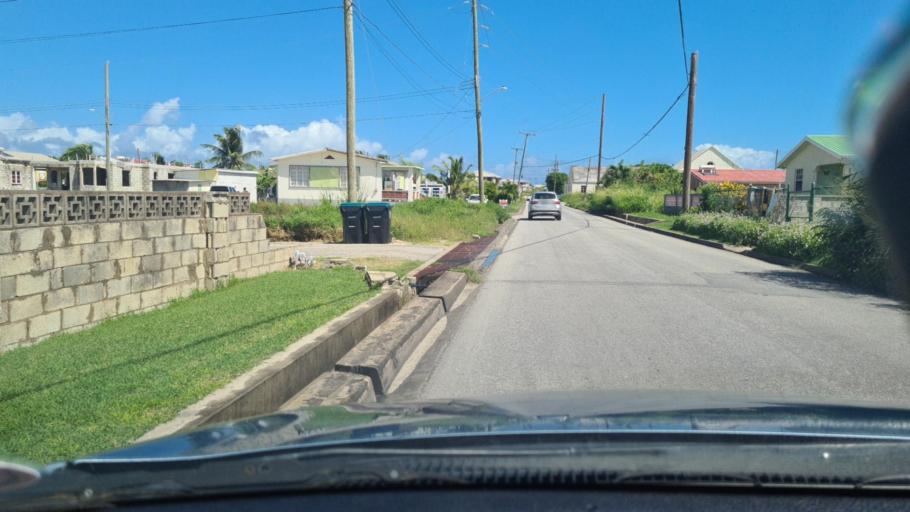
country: BB
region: Saint Philip
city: Crane
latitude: 13.1358
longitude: -59.4368
